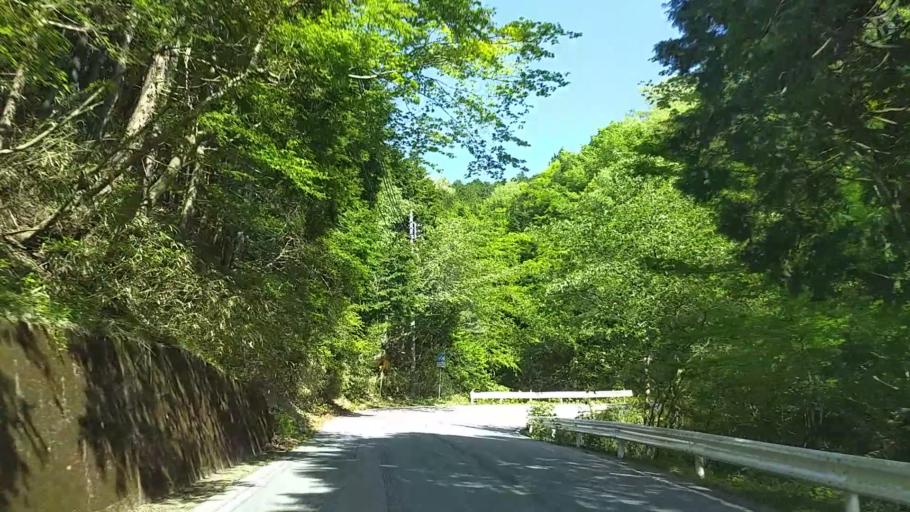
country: JP
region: Shizuoka
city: Gotemba
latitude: 35.2696
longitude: 138.9623
